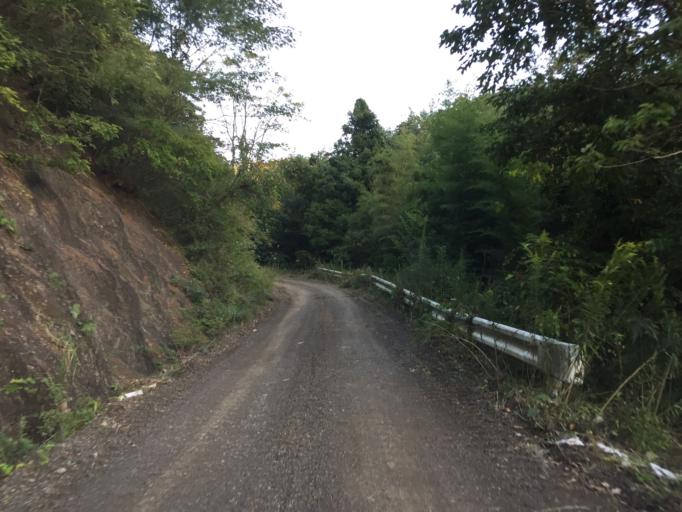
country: JP
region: Fukushima
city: Yanagawamachi-saiwaicho
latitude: 37.8431
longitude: 140.6252
